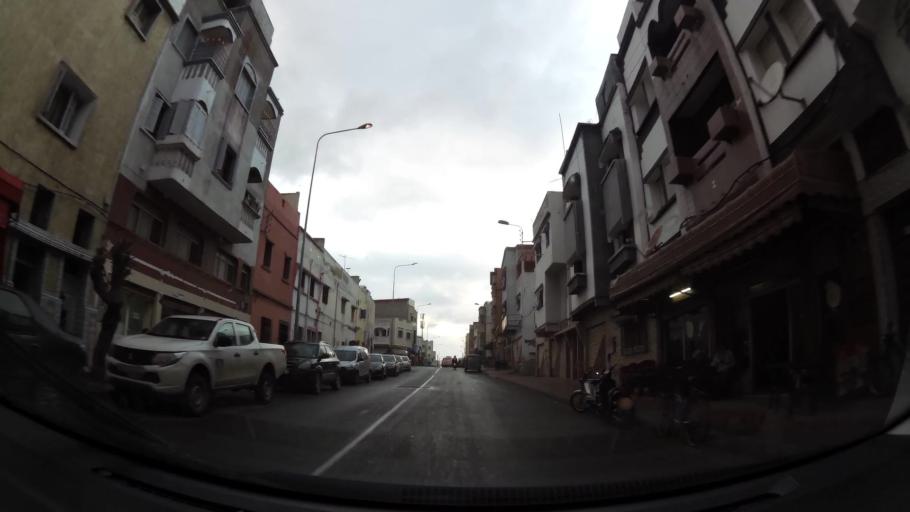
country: MA
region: Doukkala-Abda
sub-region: El-Jadida
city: El Jadida
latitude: 33.2592
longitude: -8.5102
